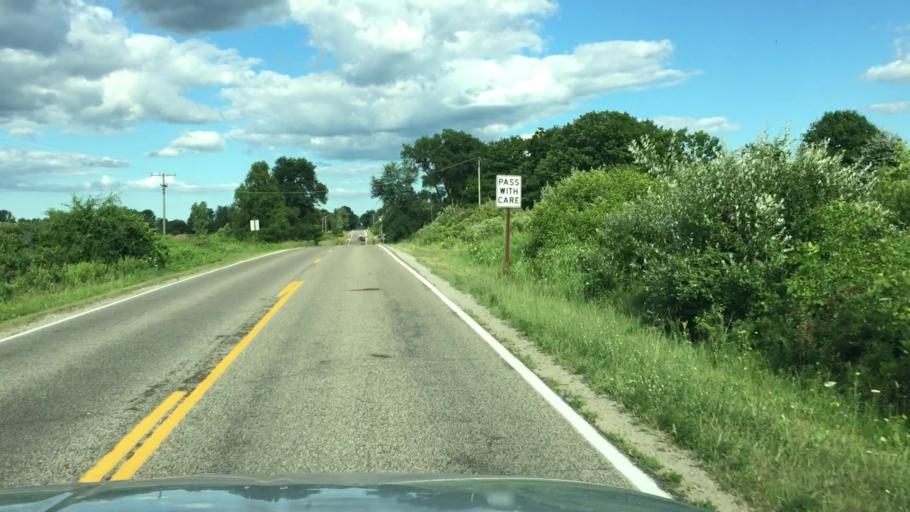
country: US
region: Michigan
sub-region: Saint Clair County
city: Yale
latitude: 43.1287
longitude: -82.8455
